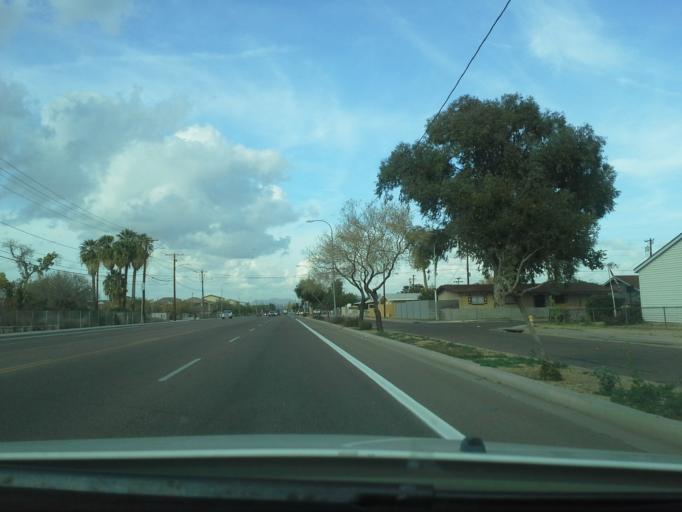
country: US
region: Arizona
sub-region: Maricopa County
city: Phoenix
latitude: 33.3794
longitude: -112.0819
